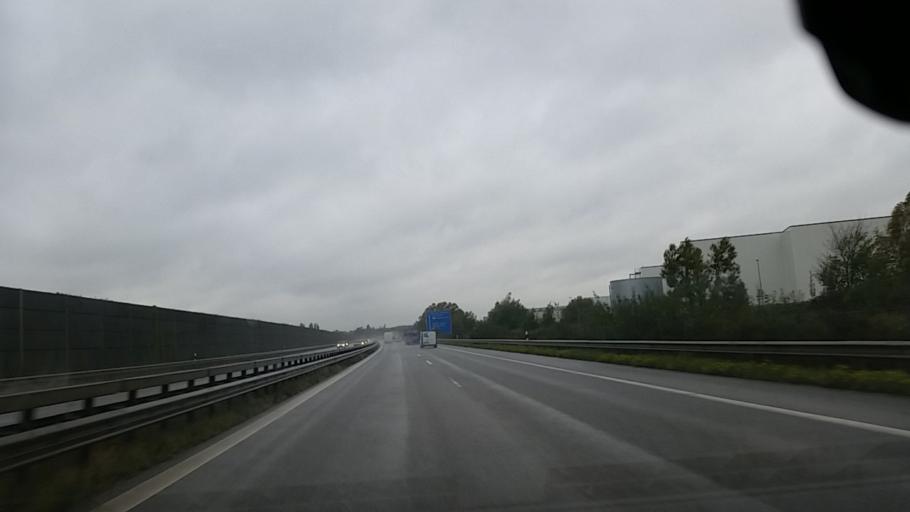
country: DE
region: Hamburg
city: Rothenburgsort
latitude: 53.4996
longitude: 10.0912
